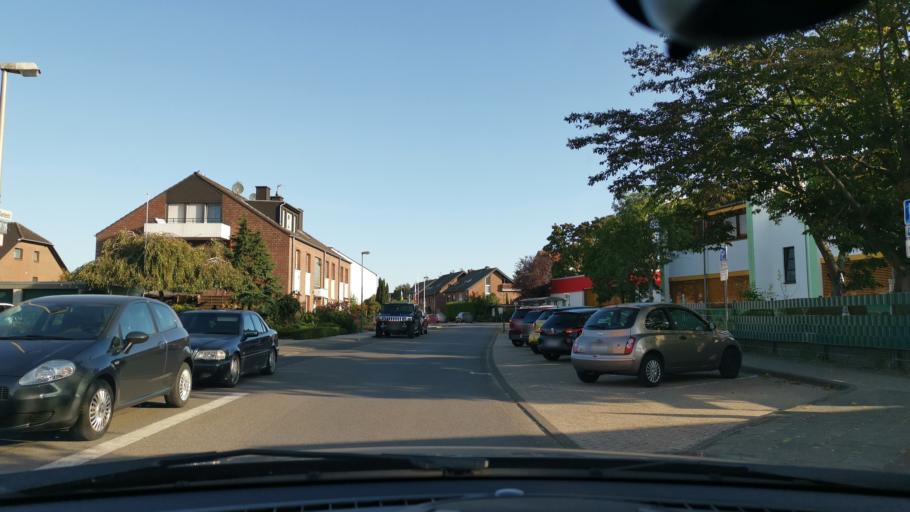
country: DE
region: North Rhine-Westphalia
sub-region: Regierungsbezirk Dusseldorf
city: Dormagen
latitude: 51.1124
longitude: 6.7573
